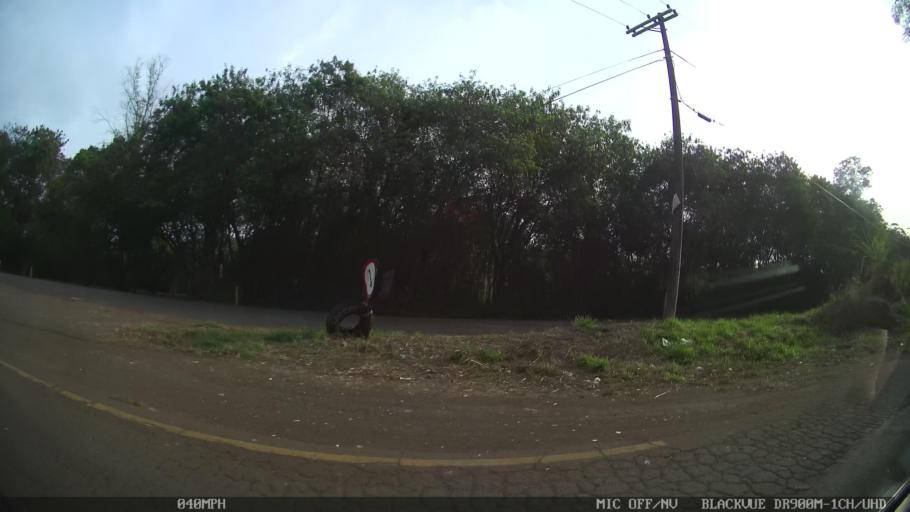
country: BR
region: Sao Paulo
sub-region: Piracicaba
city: Piracicaba
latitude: -22.7038
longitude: -47.5869
